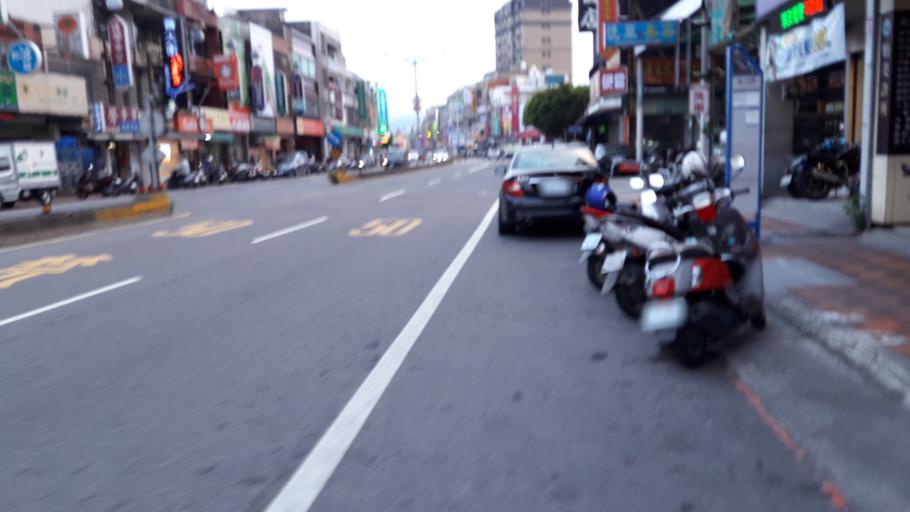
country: TW
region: Taiwan
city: Daxi
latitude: 24.8650
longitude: 121.2170
